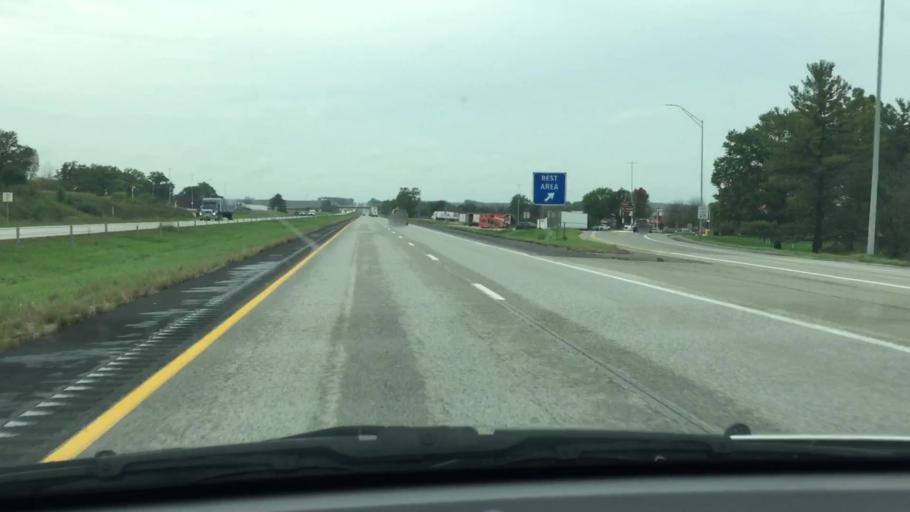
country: US
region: Iowa
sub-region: Johnson County
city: Tiffin
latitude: 41.6943
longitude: -91.6775
